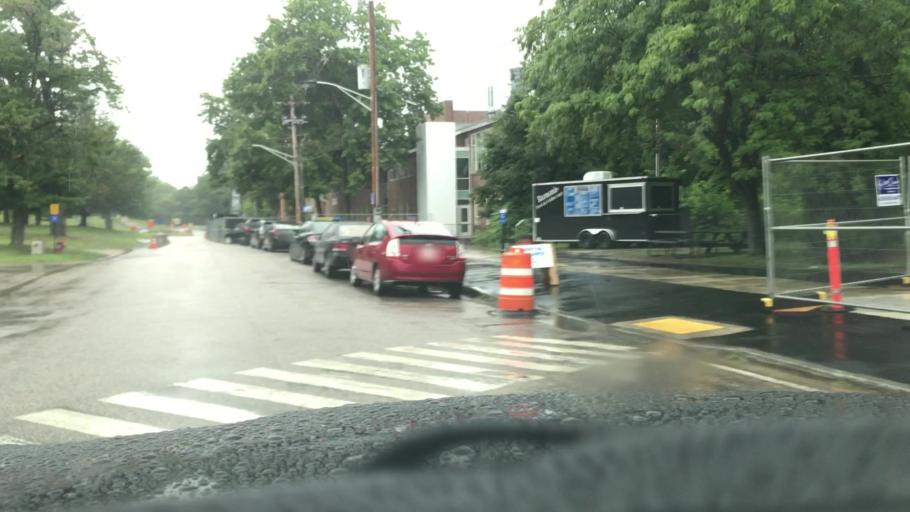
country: US
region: New Hampshire
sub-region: Strafford County
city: Durham
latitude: 43.1333
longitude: -70.9325
